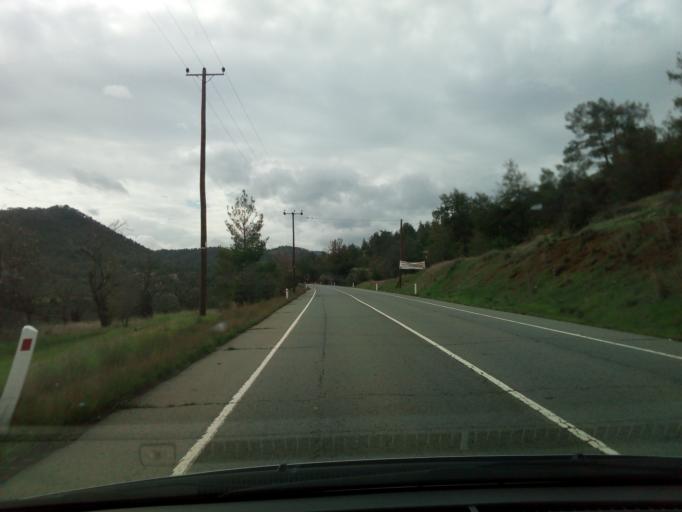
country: CY
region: Lefkosia
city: Klirou
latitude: 35.0064
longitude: 33.1450
